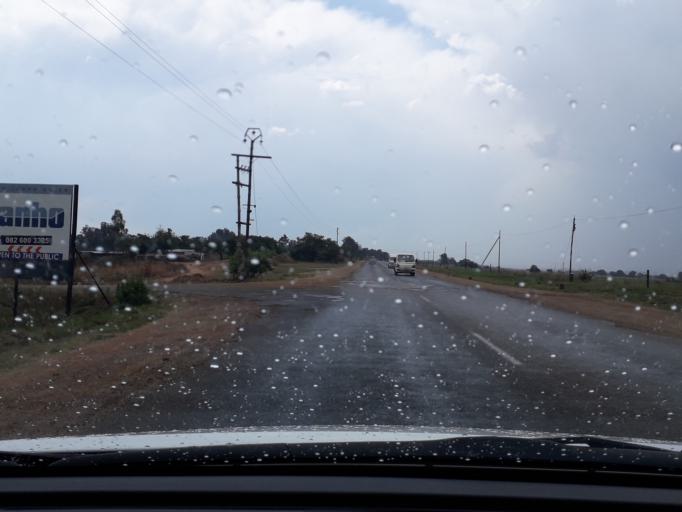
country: ZA
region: Gauteng
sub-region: West Rand District Municipality
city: Muldersdriseloop
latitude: -26.0046
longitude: 27.8580
